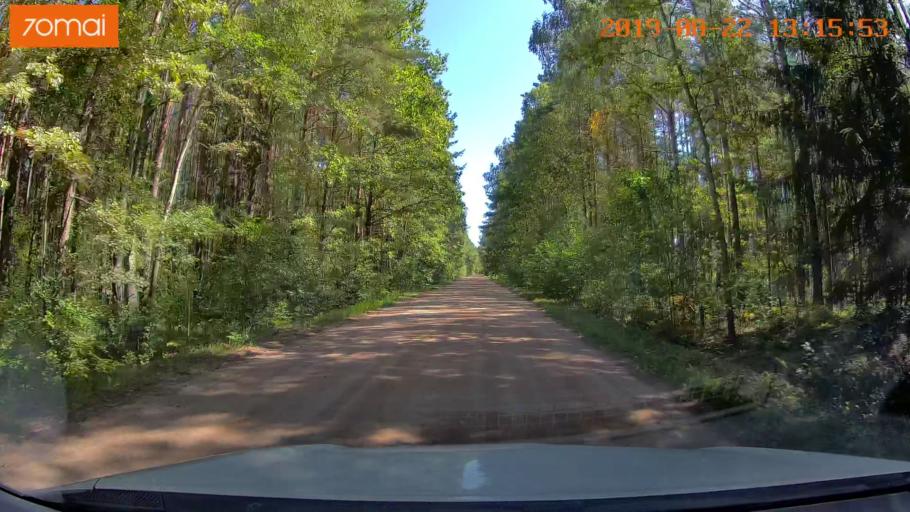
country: BY
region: Minsk
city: Prawdzinski
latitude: 53.2579
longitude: 27.9033
